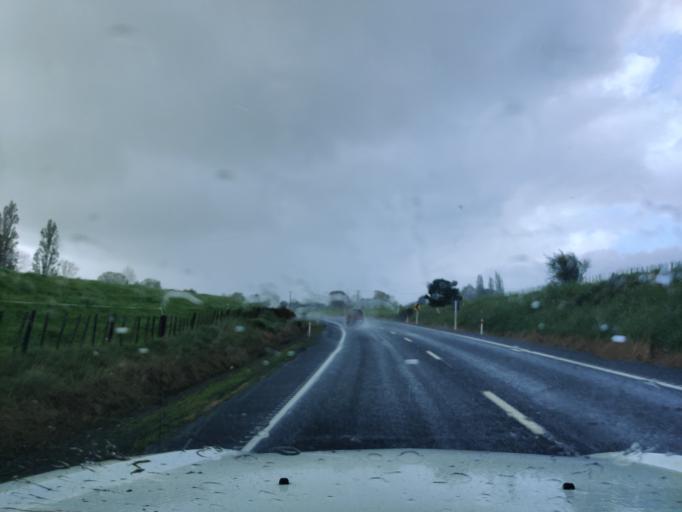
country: NZ
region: Waikato
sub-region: Matamata-Piako District
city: Matamata
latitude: -37.9824
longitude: 175.7041
